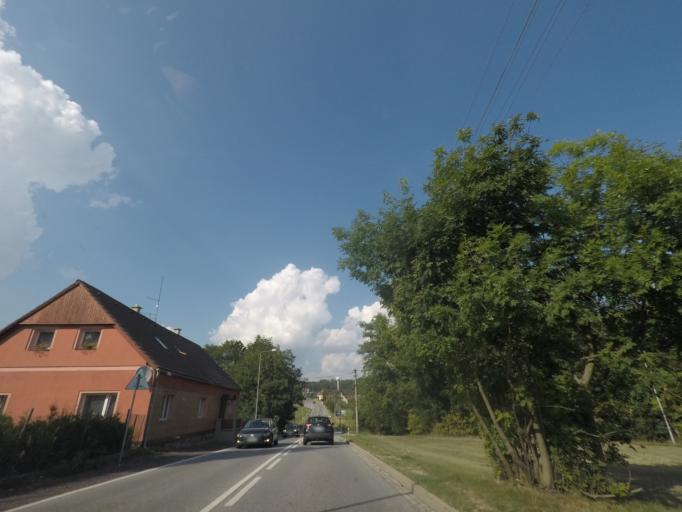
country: CZ
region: Kralovehradecky
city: Dvur Kralove nad Labem
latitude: 50.4579
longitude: 15.8593
